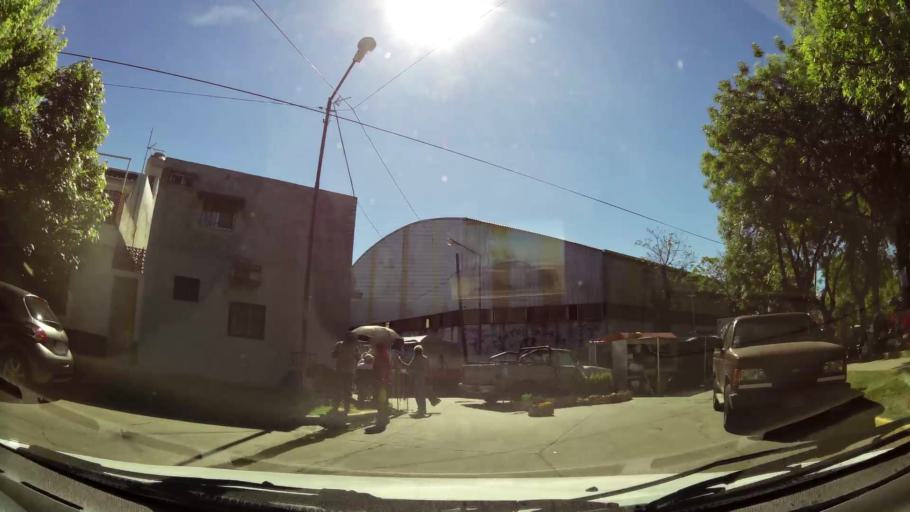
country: AR
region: Buenos Aires
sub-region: Partido de General San Martin
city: General San Martin
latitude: -34.5449
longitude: -58.5307
